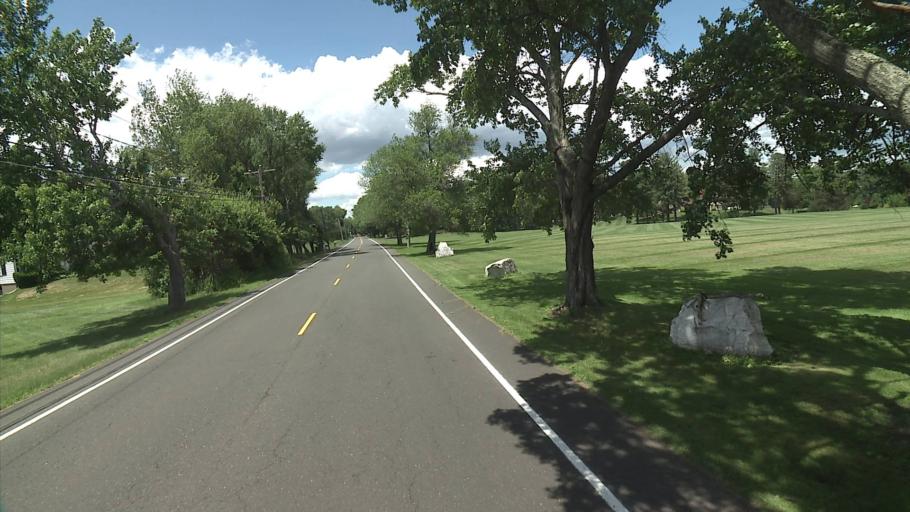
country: US
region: Massachusetts
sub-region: Hampden County
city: East Longmeadow
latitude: 42.0289
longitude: -72.4882
